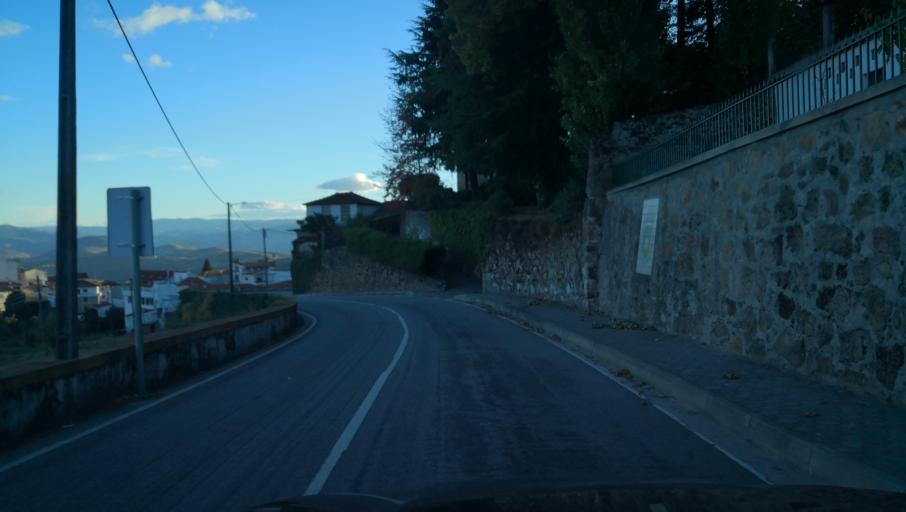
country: PT
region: Vila Real
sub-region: Santa Marta de Penaguiao
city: Santa Marta de Penaguiao
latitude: 41.2551
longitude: -7.7716
